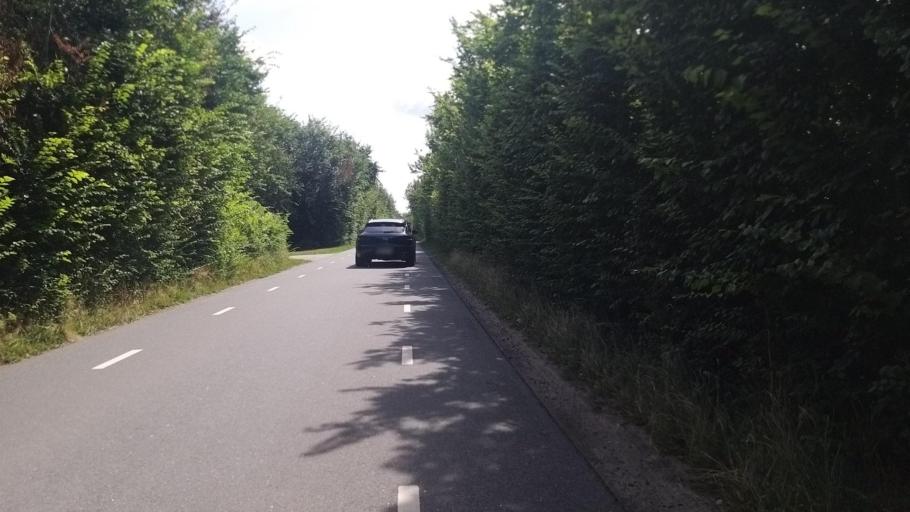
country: NL
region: North Holland
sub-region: Gemeente Texel
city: Den Burg
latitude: 53.0878
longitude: 4.7811
